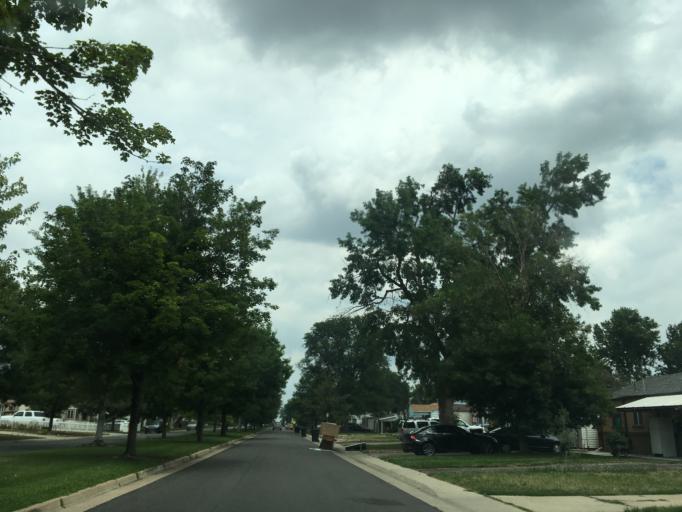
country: US
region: Colorado
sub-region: Arapahoe County
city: Sheridan
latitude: 39.6796
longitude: -105.0298
